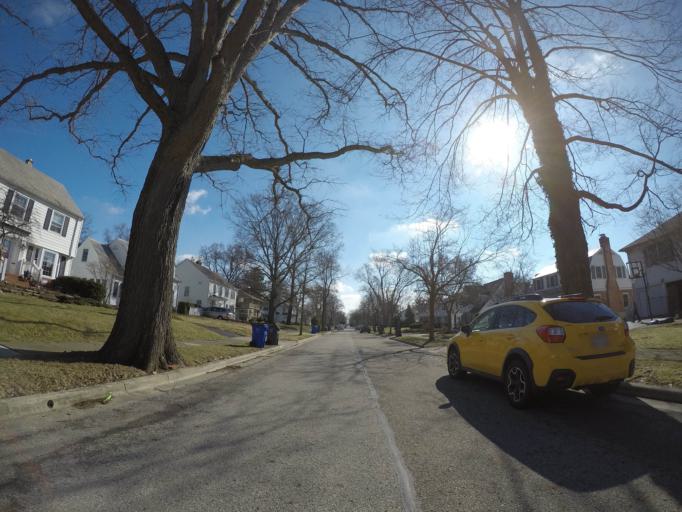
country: US
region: Ohio
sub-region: Franklin County
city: Upper Arlington
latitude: 40.0036
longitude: -83.0560
